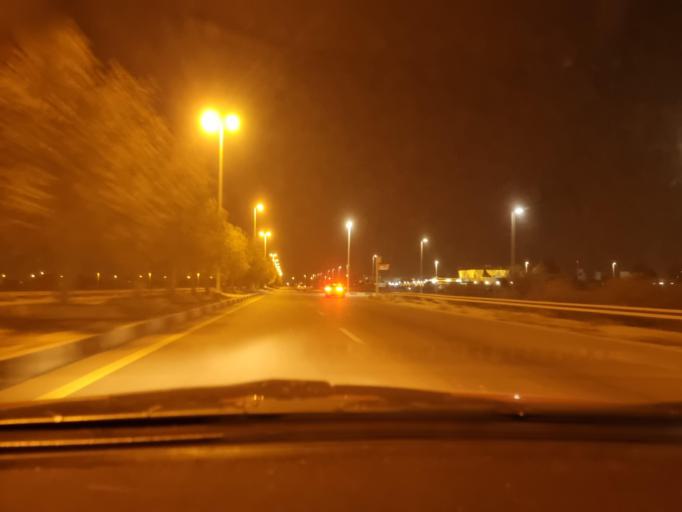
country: AE
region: Abu Dhabi
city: Abu Dhabi
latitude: 24.3831
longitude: 54.6842
